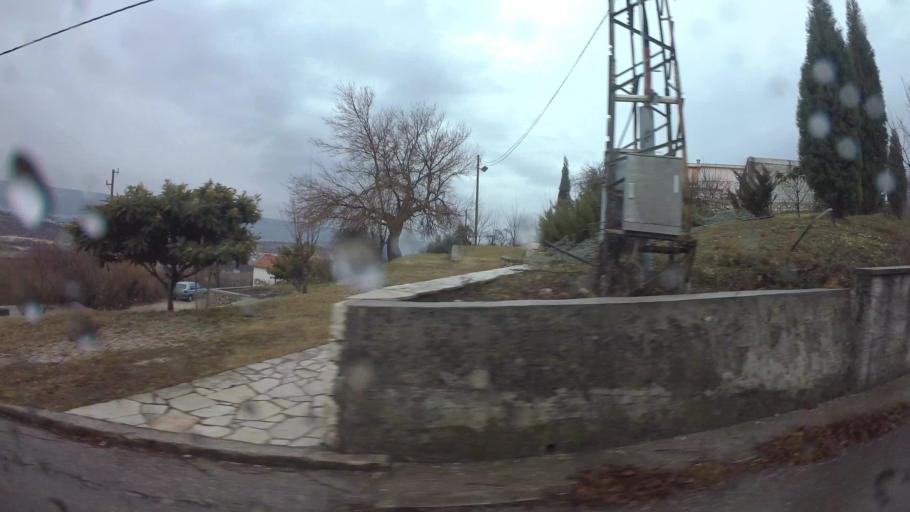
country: BA
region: Federation of Bosnia and Herzegovina
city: Blagaj
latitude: 43.2945
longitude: 17.8569
